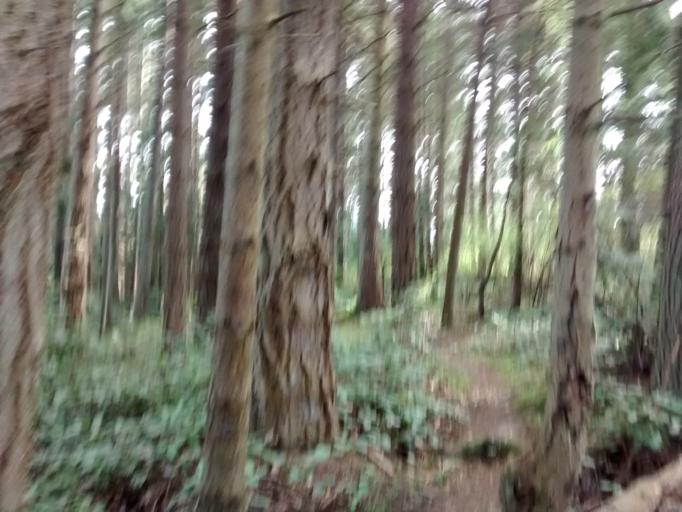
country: US
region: Washington
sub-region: Clallam County
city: Port Angeles
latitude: 48.1194
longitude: -123.4798
